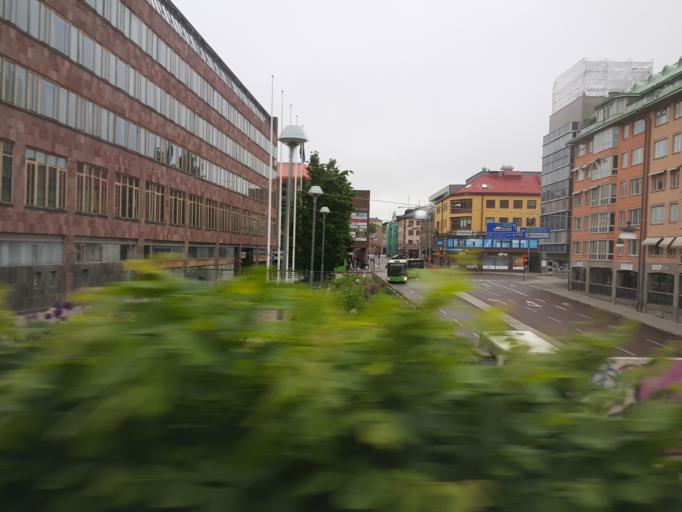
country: SE
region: Uppsala
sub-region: Uppsala Kommun
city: Uppsala
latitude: 59.8604
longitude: 17.6434
